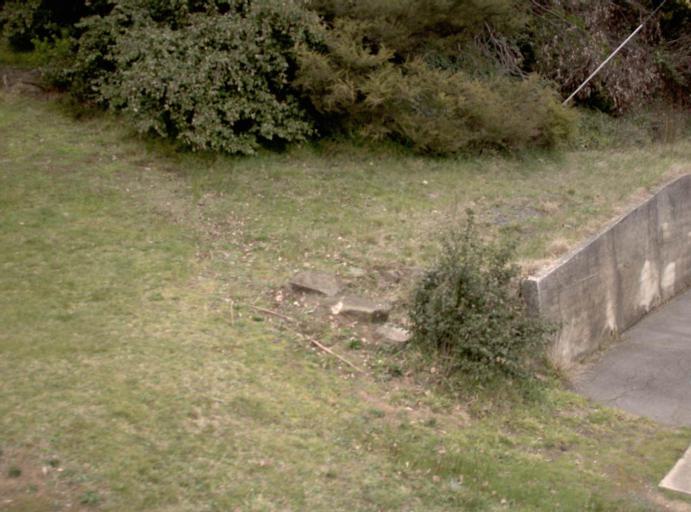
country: AU
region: Tasmania
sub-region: Launceston
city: Newstead
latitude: -41.4514
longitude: 147.1735
